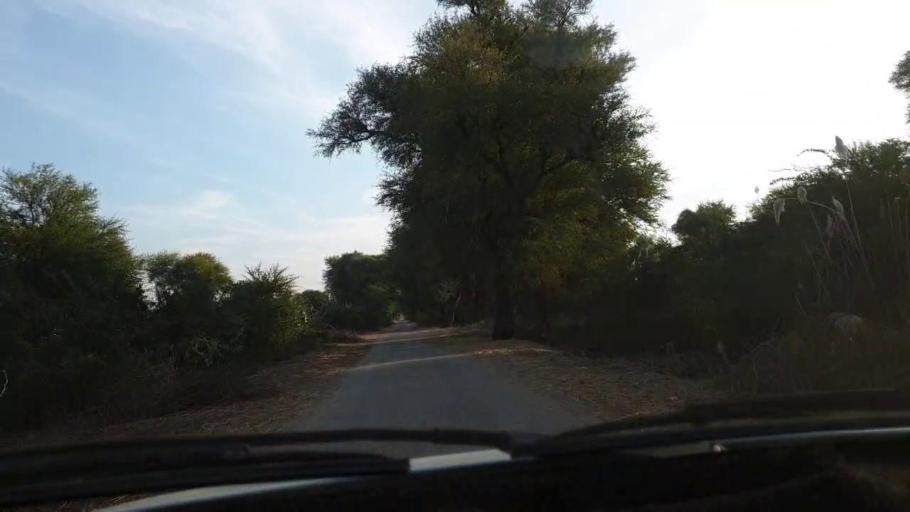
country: PK
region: Sindh
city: Bulri
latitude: 25.0235
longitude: 68.2886
